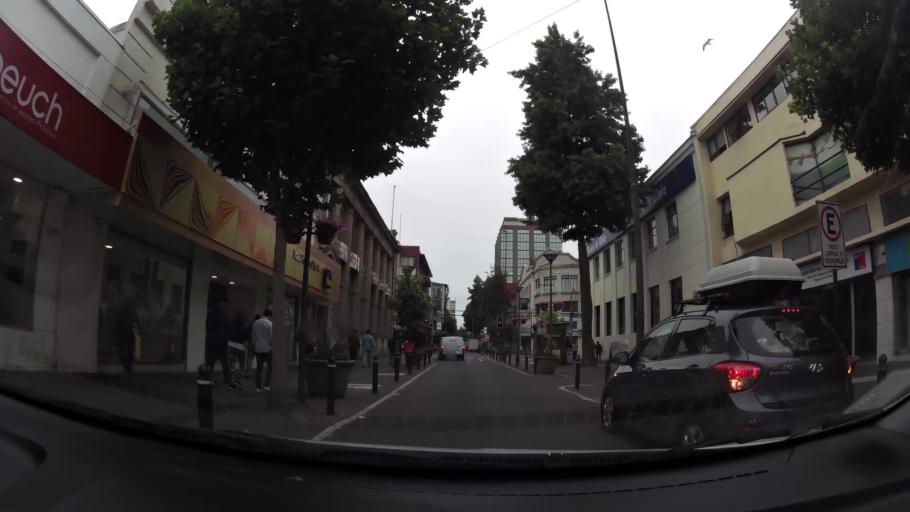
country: CL
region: Biobio
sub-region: Provincia de Concepcion
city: Concepcion
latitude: -36.8280
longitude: -73.0542
